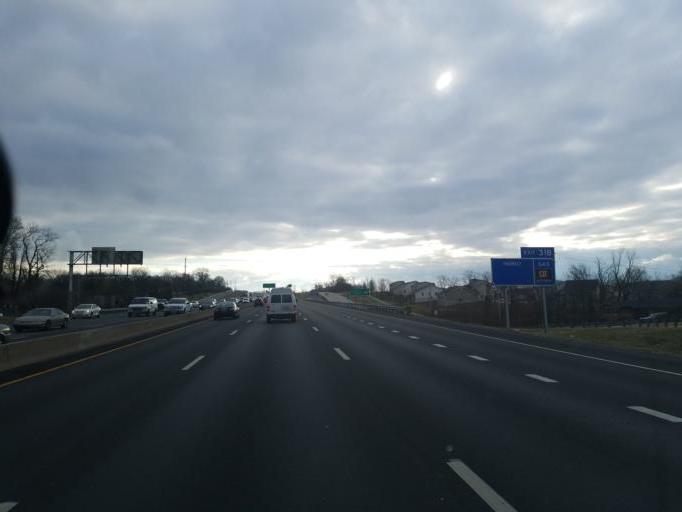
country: US
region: Missouri
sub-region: Saint Louis County
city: Castle Point
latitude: 38.7713
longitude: -90.2515
